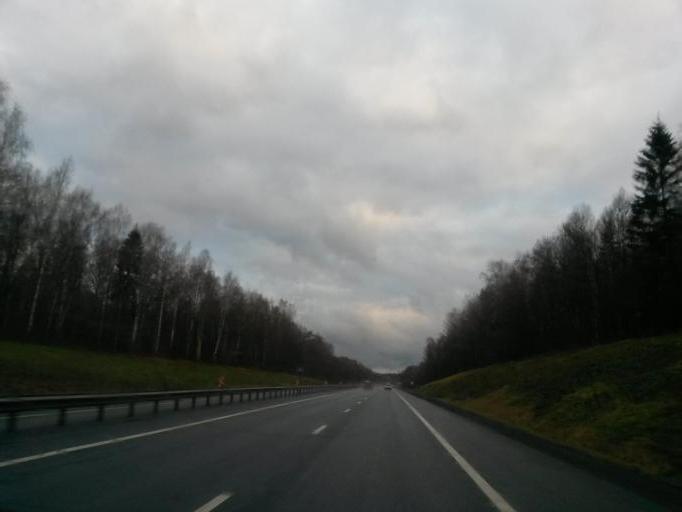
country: RU
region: Moskovskaya
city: Krasnozavodsk
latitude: 56.4430
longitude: 38.3468
